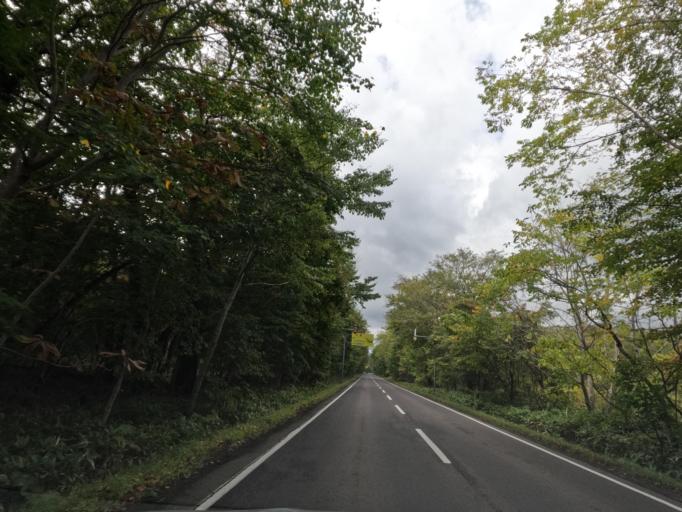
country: JP
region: Hokkaido
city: Chitose
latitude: 42.7928
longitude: 141.5142
